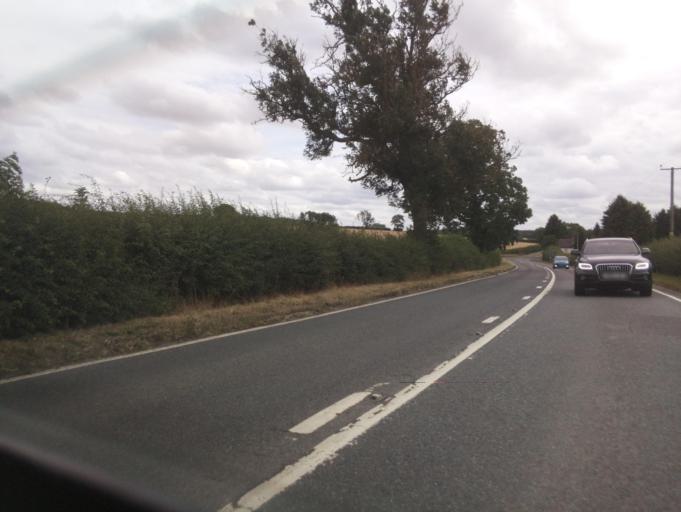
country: GB
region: England
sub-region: Leicestershire
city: Castle Donington
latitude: 52.8174
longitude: -1.3780
